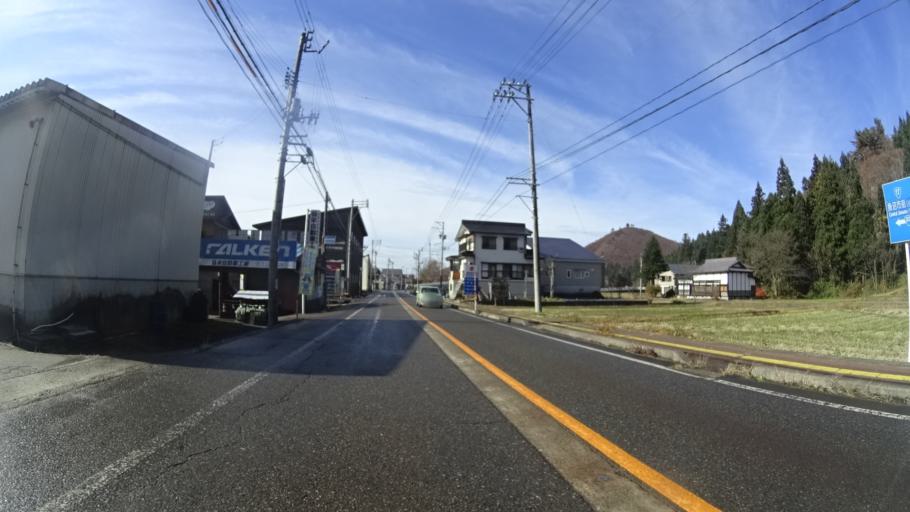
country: JP
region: Niigata
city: Muikamachi
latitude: 37.2255
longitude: 139.0108
